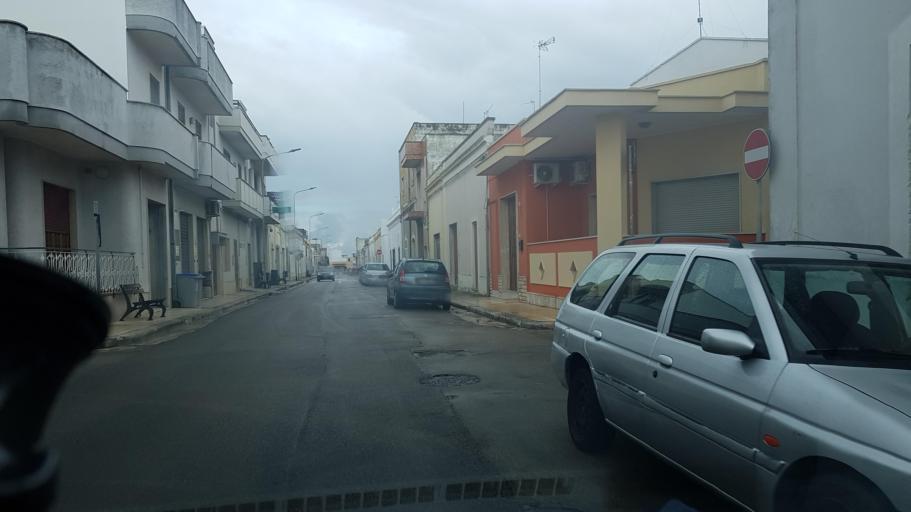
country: IT
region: Apulia
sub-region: Provincia di Lecce
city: Carmiano
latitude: 40.3457
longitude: 18.0424
